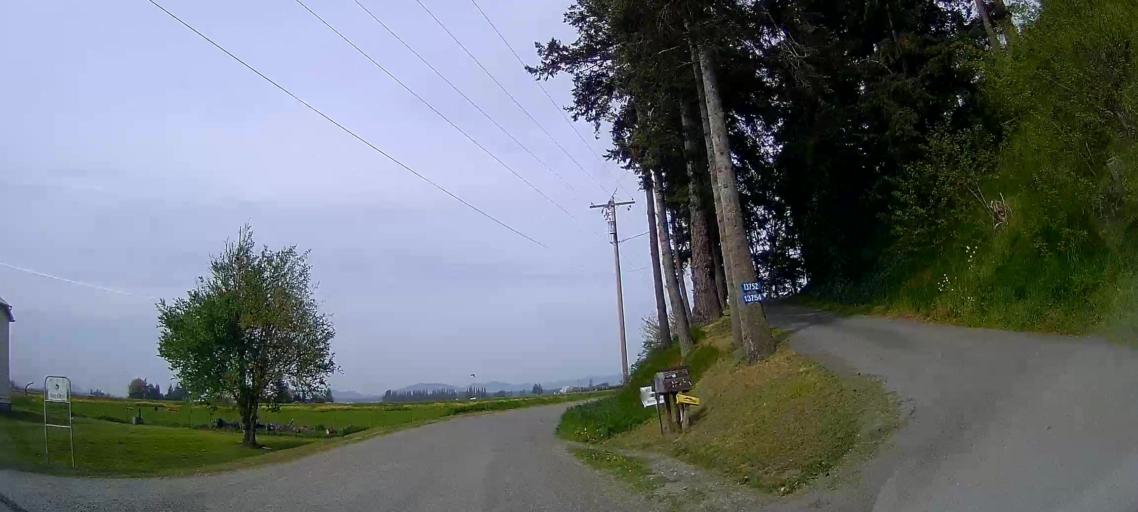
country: US
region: Washington
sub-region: Skagit County
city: Mount Vernon
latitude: 48.3947
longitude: -122.4485
